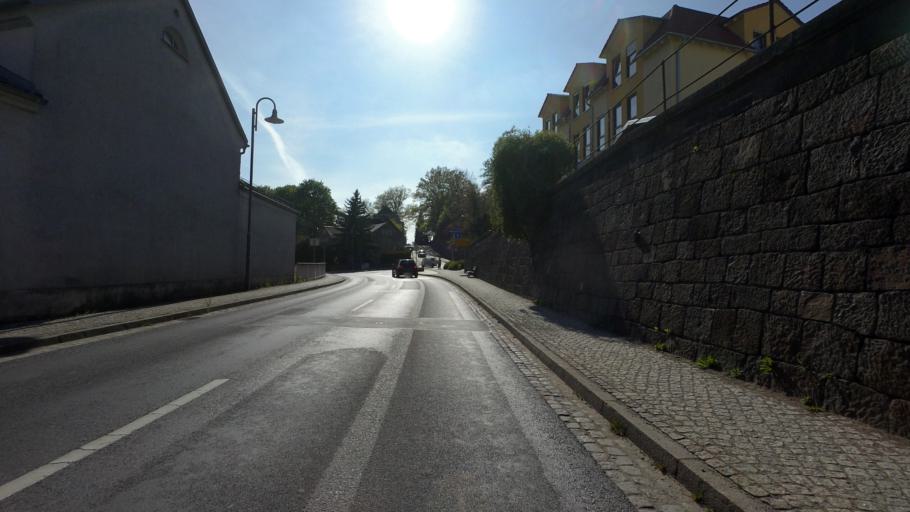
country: DE
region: Saxony
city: Grossrohrsdorf
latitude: 51.1443
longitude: 14.0182
